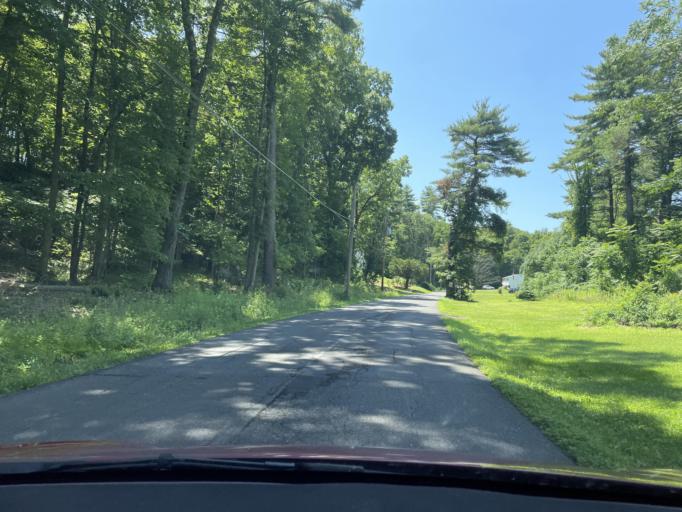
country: US
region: New York
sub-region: Ulster County
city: Glasco
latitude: 42.0269
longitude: -73.9732
